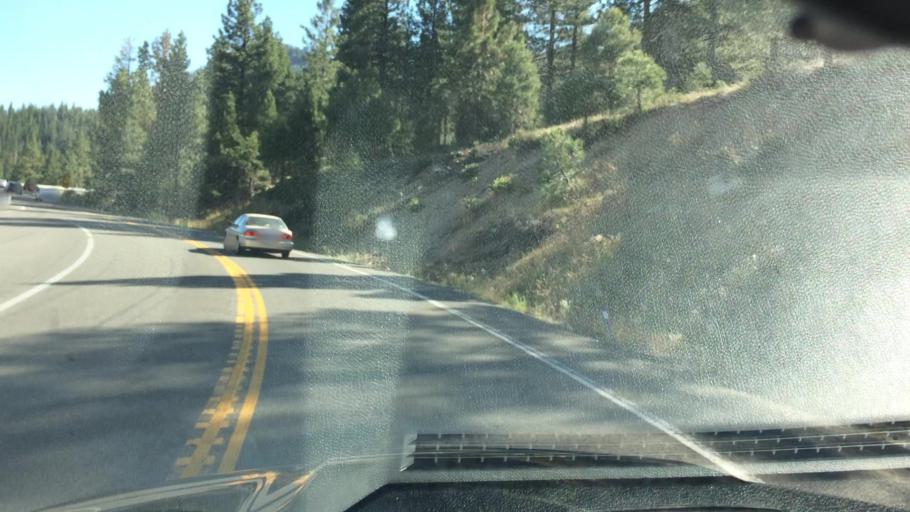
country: US
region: Nevada
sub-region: Washoe County
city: Incline Village
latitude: 39.3393
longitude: -119.8608
